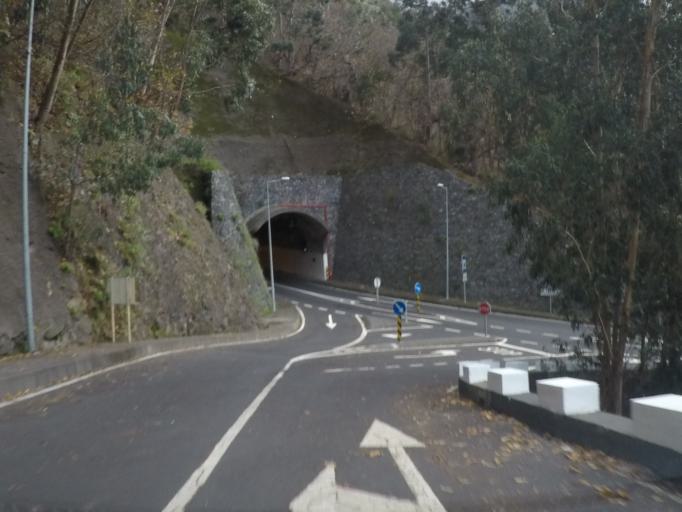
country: PT
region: Madeira
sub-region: Camara de Lobos
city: Curral das Freiras
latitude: 32.7245
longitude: -16.9622
